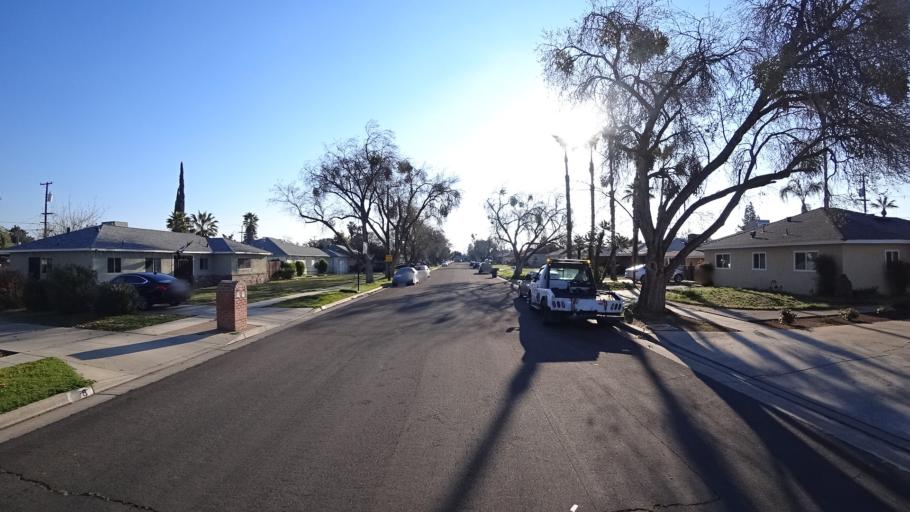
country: US
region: California
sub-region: Fresno County
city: Fresno
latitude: 36.8130
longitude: -119.7797
